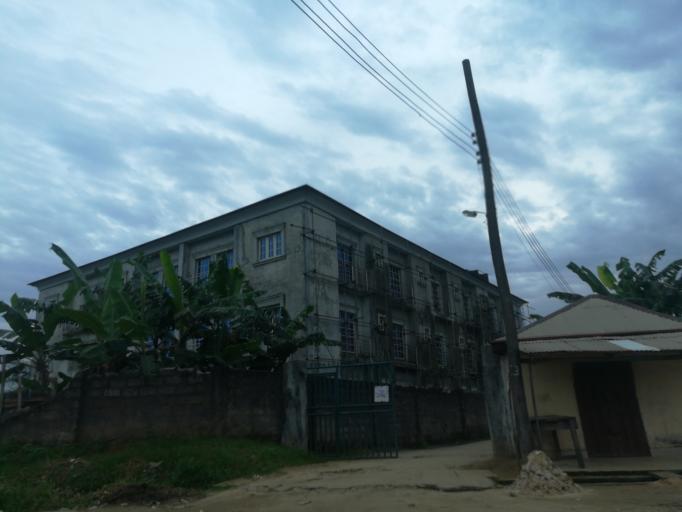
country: NG
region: Rivers
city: Port Harcourt
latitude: 4.7952
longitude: 6.9554
